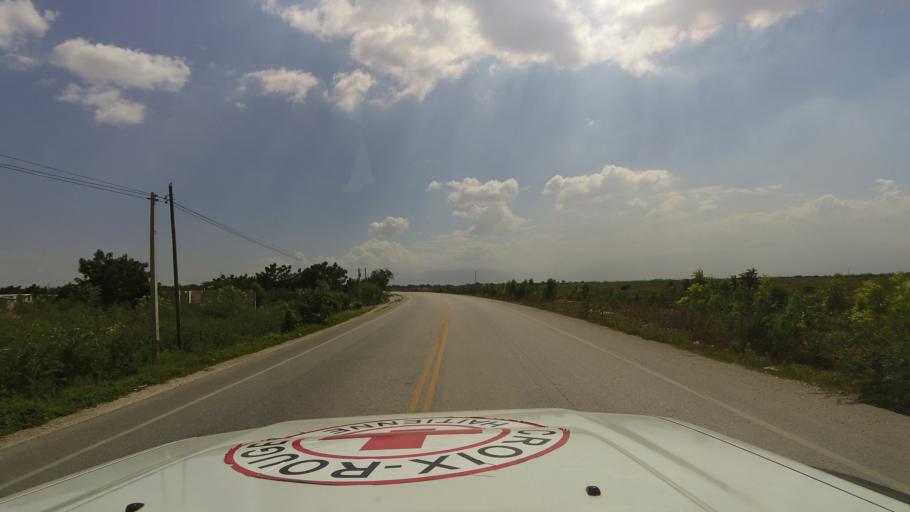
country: HT
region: Ouest
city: Croix des Bouquets
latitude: 18.6518
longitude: -72.2850
